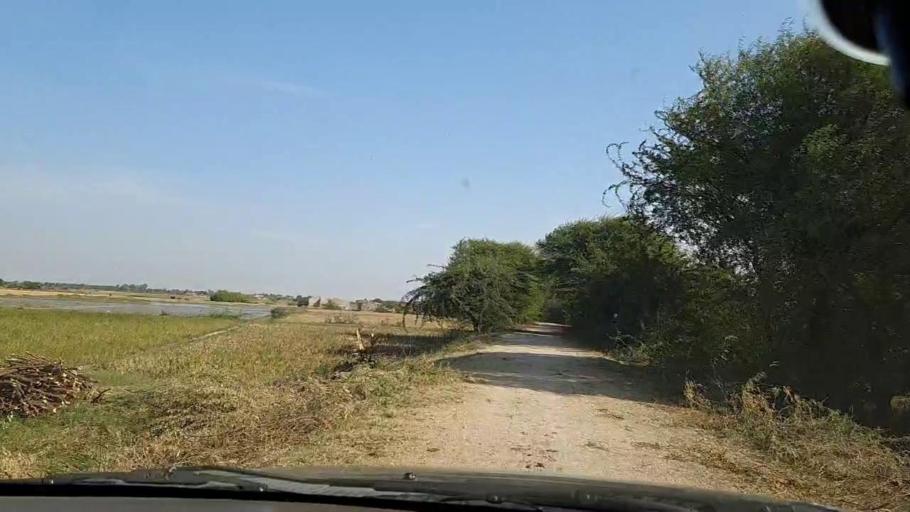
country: PK
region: Sindh
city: Mirpur Batoro
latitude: 24.6294
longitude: 68.2663
